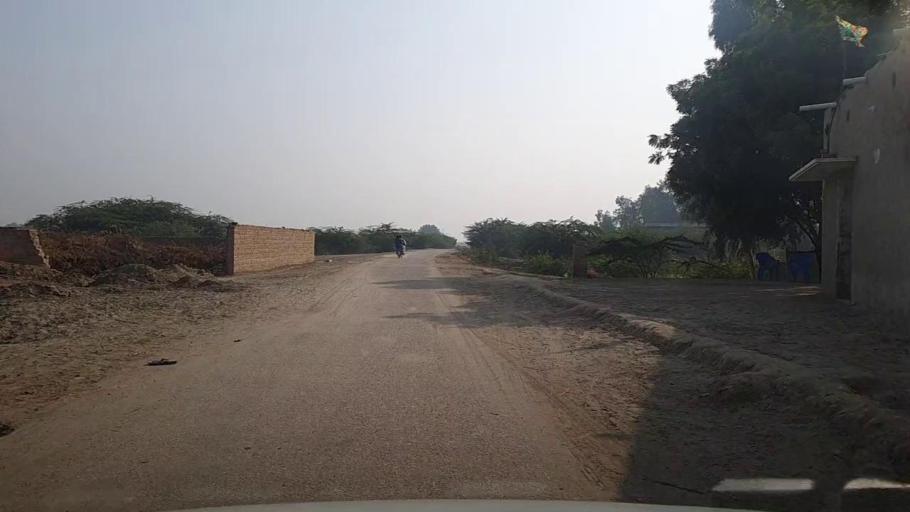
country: PK
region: Sindh
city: Kandiari
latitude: 27.0540
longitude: 68.4617
